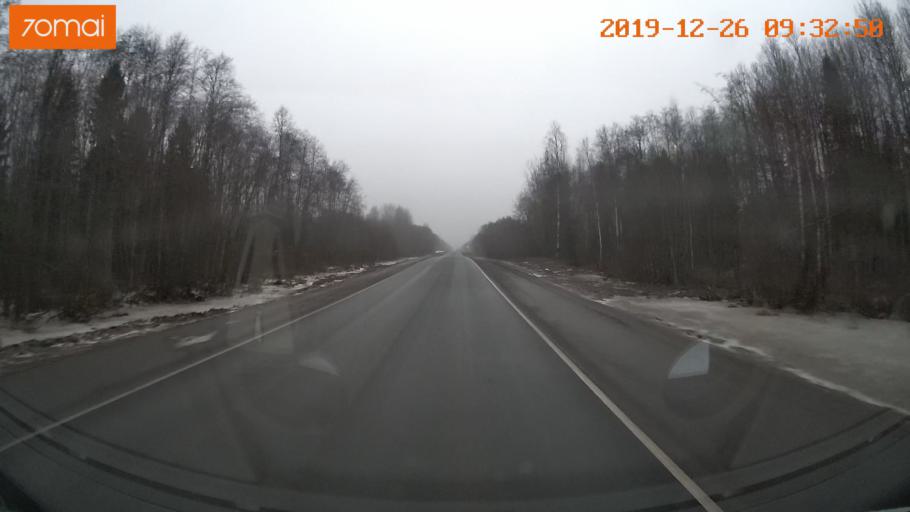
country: RU
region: Vologda
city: Gryazovets
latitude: 59.0826
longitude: 40.1103
